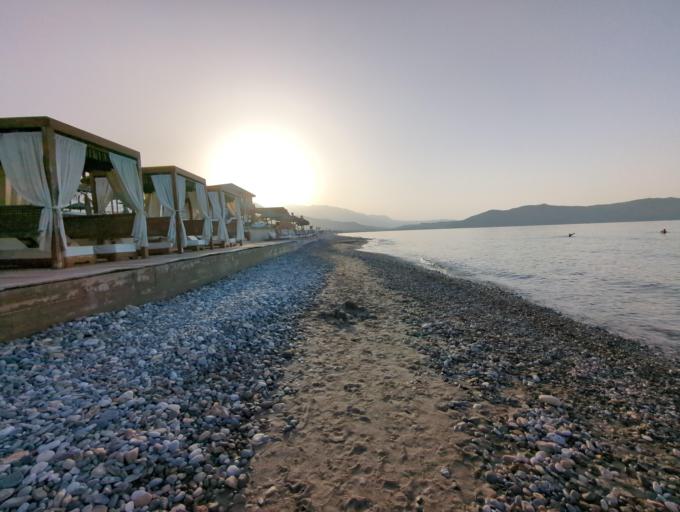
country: GR
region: Crete
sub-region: Nomos Chanias
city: Georgioupolis
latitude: 35.3530
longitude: 24.3104
